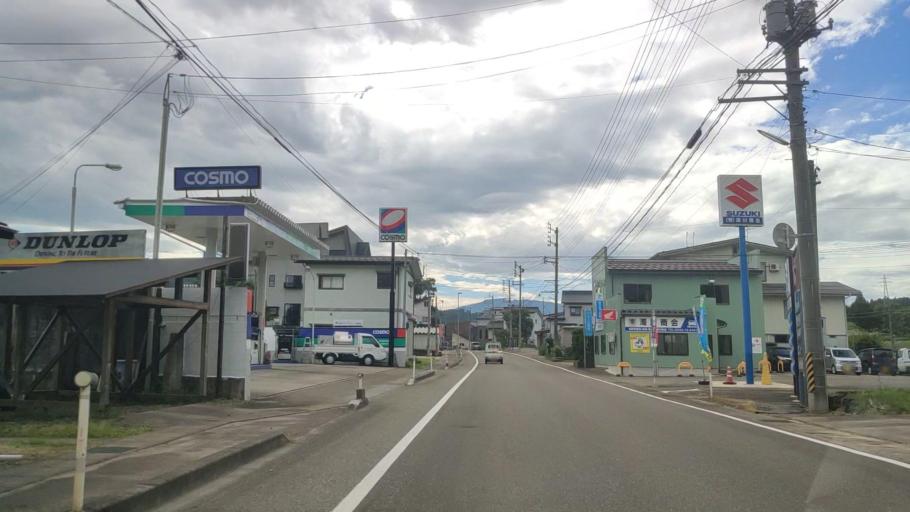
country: JP
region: Niigata
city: Arai
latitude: 36.9908
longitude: 138.2704
